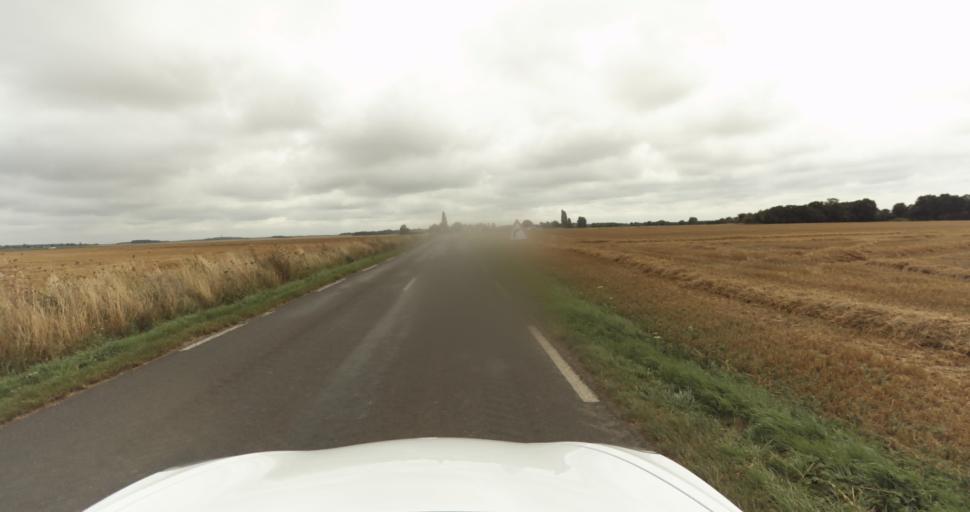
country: FR
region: Haute-Normandie
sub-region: Departement de l'Eure
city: Claville
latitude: 49.0743
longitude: 1.0645
